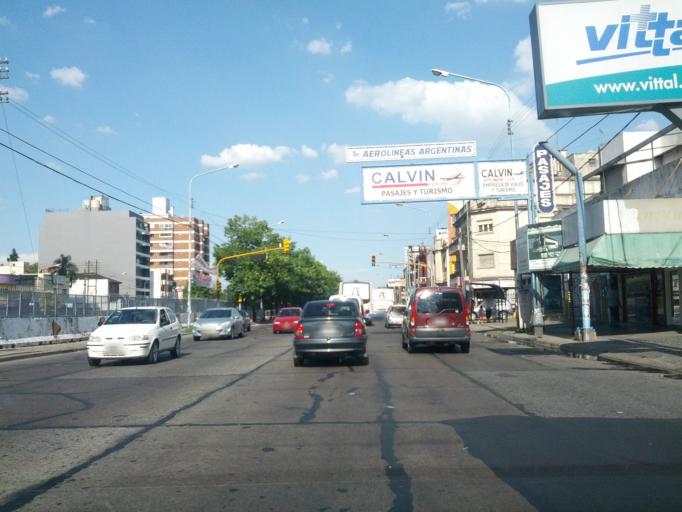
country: AR
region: Buenos Aires
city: San Justo
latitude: -34.6401
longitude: -58.5608
